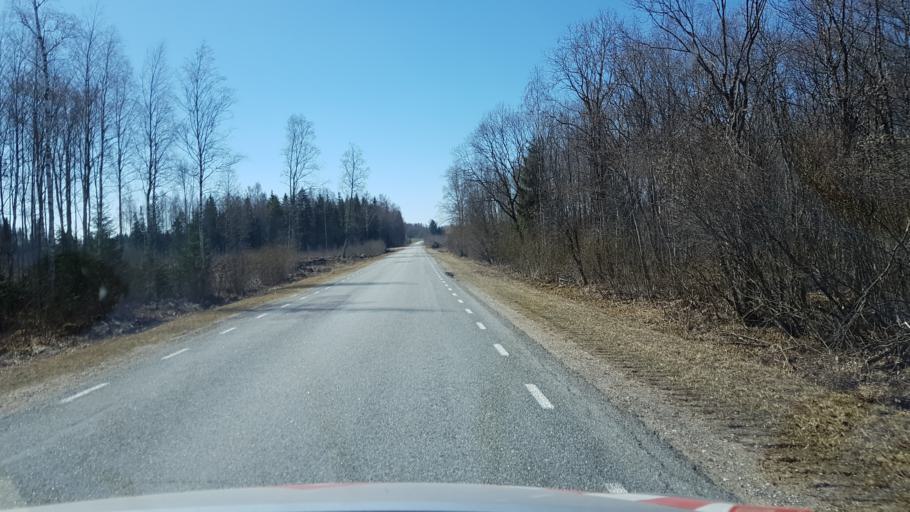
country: EE
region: Laeaene-Virumaa
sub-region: Rakke vald
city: Rakke
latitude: 59.0142
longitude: 26.3419
